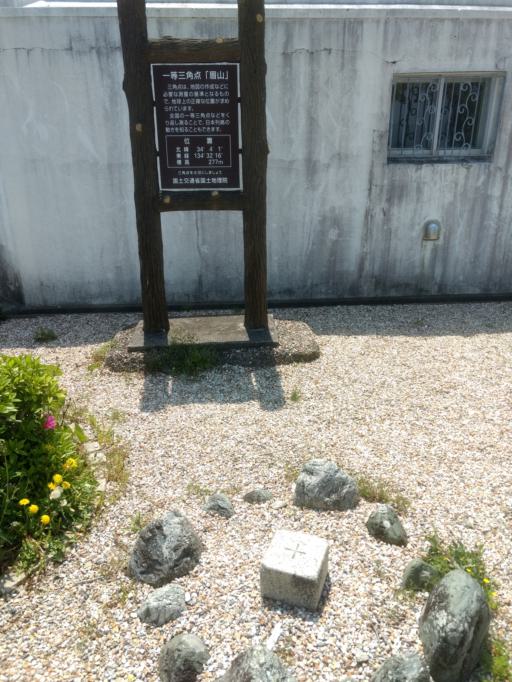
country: JP
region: Tokushima
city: Tokushima-shi
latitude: 34.0671
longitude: 134.5376
